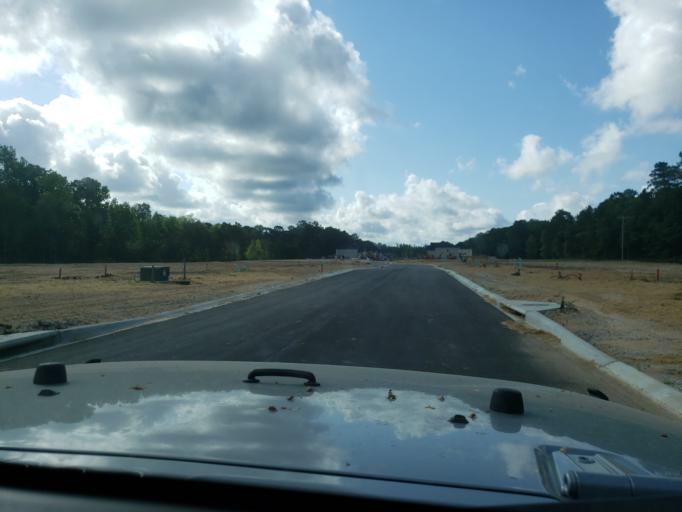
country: US
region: Georgia
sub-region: Chatham County
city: Georgetown
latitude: 32.0417
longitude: -81.2258
